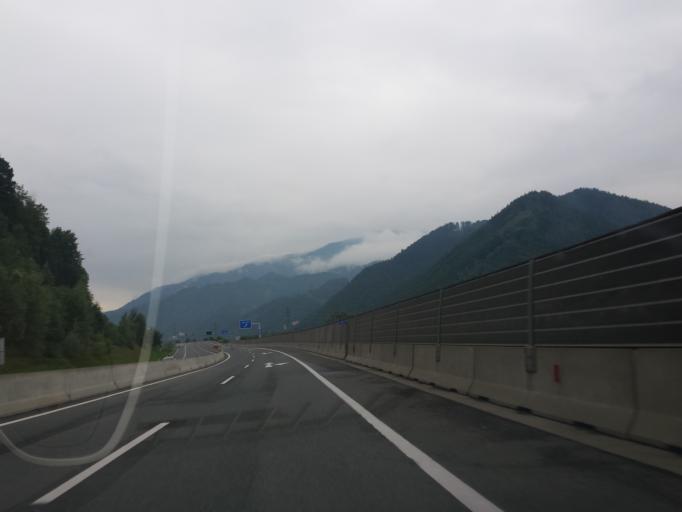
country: AT
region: Styria
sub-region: Politischer Bezirk Bruck-Muerzzuschlag
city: Pernegg an der Mur
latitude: 47.3381
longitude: 15.3511
